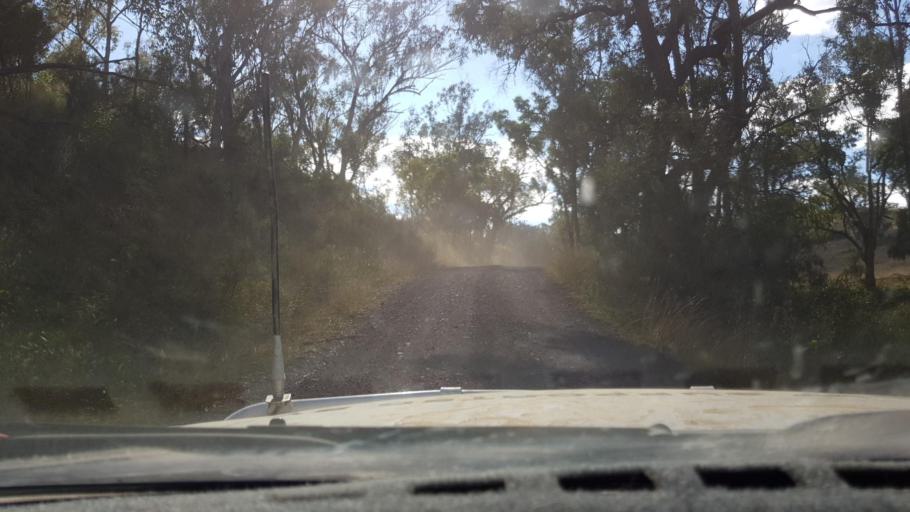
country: AU
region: New South Wales
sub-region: Tamworth Municipality
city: Manilla
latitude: -30.4782
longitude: 150.7723
